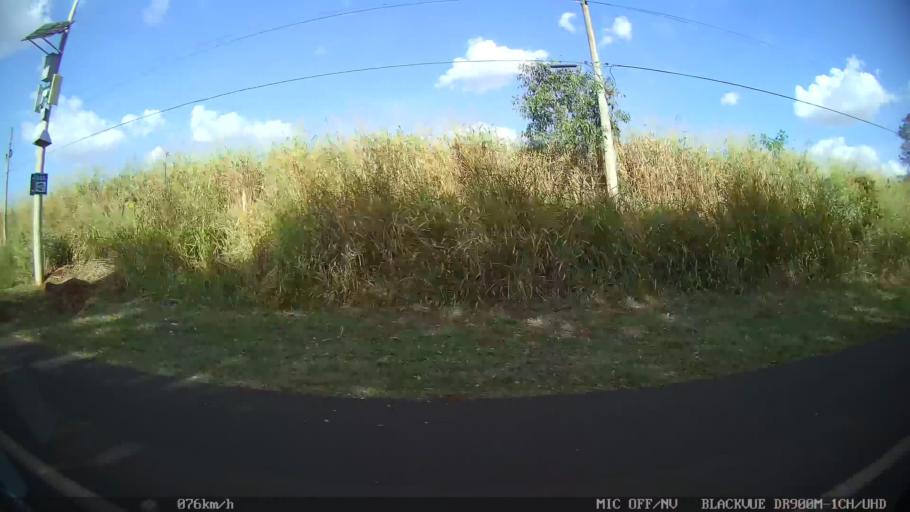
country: BR
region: Sao Paulo
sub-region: Ribeirao Preto
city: Ribeirao Preto
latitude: -21.1807
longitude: -47.8572
